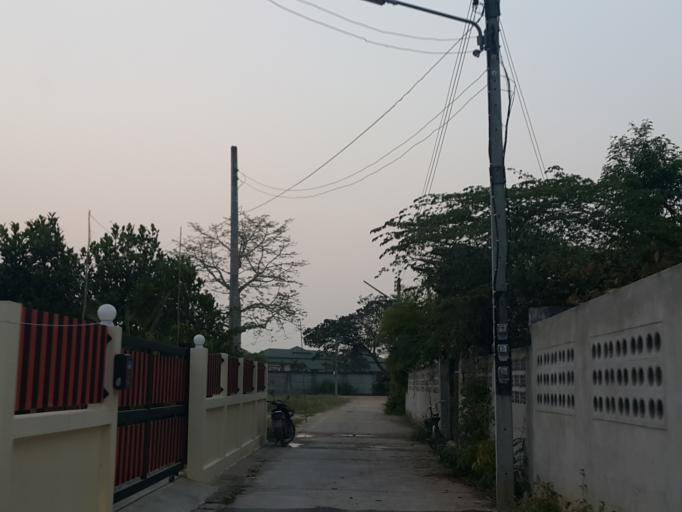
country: TH
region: Chiang Mai
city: San Kamphaeng
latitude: 18.7744
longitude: 99.0745
